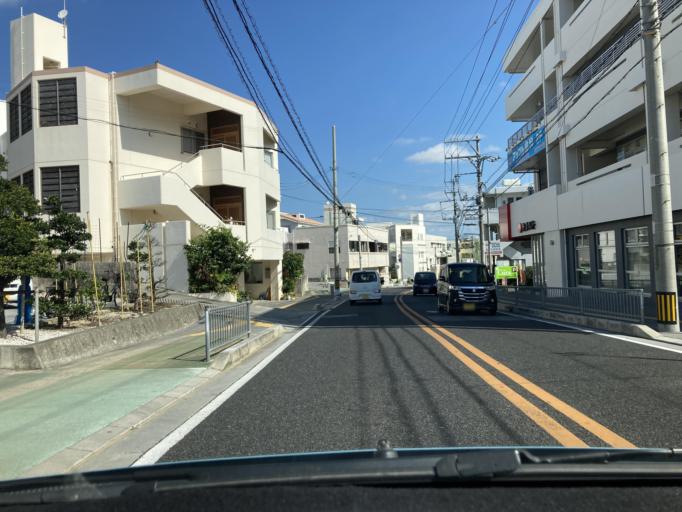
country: JP
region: Okinawa
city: Tomigusuku
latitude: 26.1896
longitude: 127.6688
